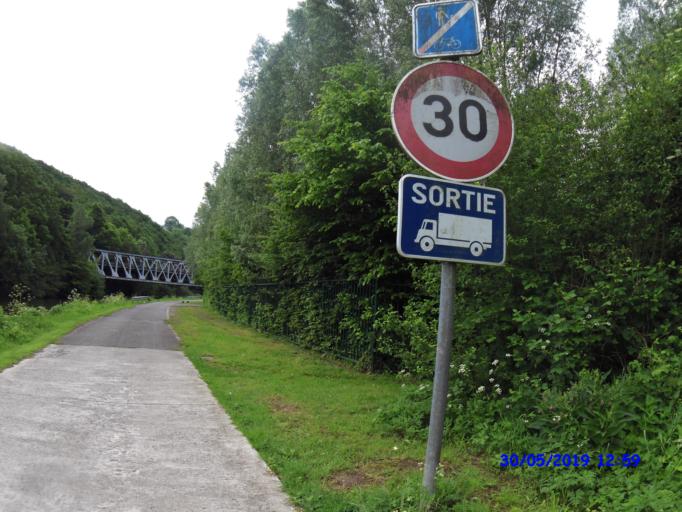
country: BE
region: Wallonia
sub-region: Province du Hainaut
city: Thuin
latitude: 50.3463
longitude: 4.2946
